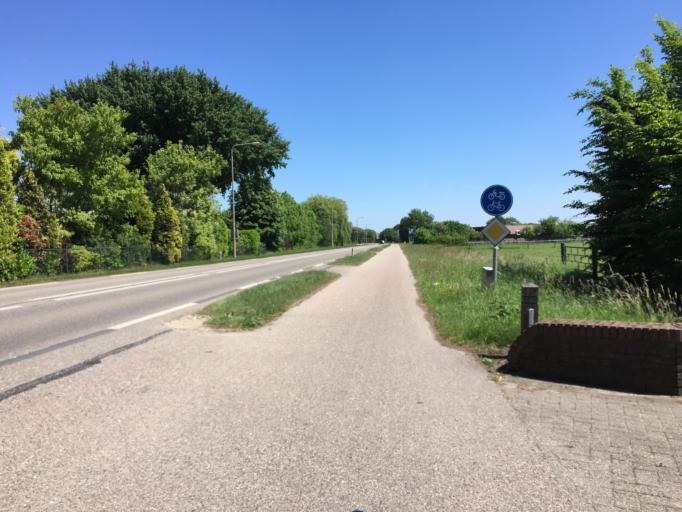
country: NL
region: Gelderland
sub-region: Gemeente Maasdriel
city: Hedel
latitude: 51.7484
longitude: 5.2401
